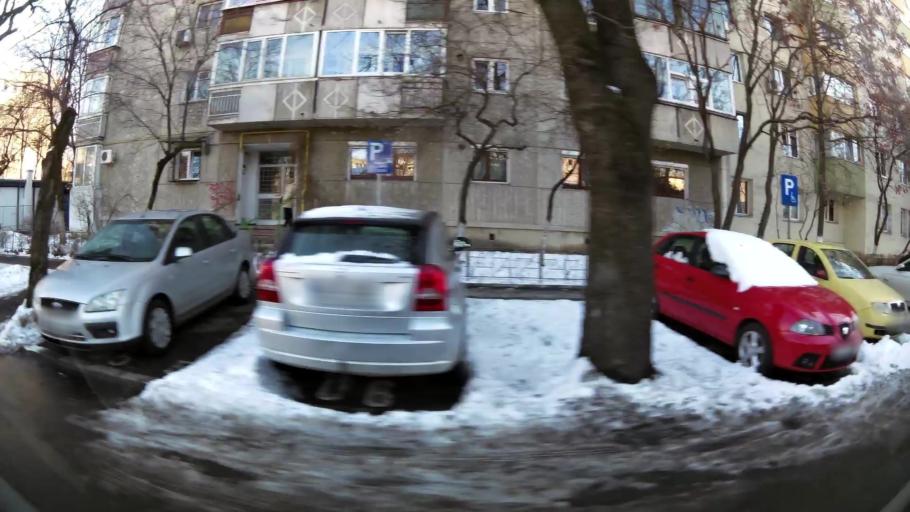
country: RO
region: Bucuresti
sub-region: Municipiul Bucuresti
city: Bucharest
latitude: 44.4619
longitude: 26.1254
